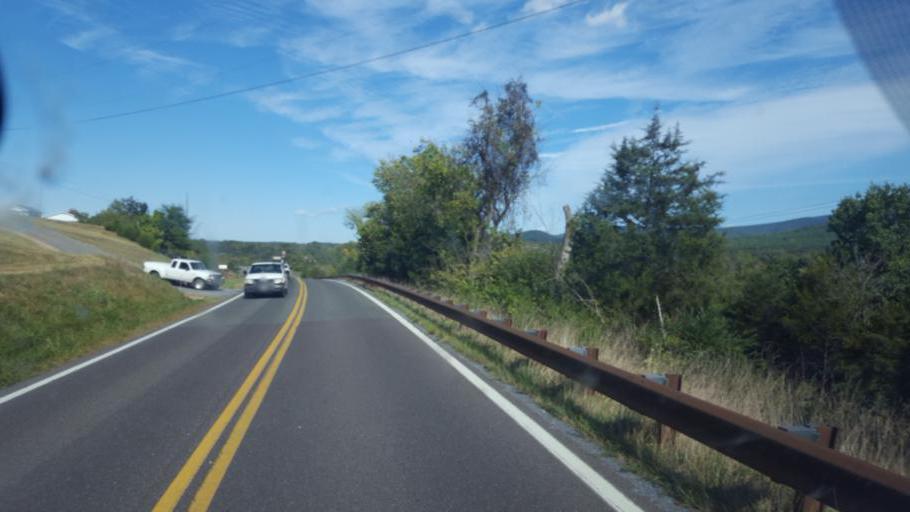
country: US
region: Virginia
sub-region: Page County
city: Luray
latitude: 38.7617
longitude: -78.3964
